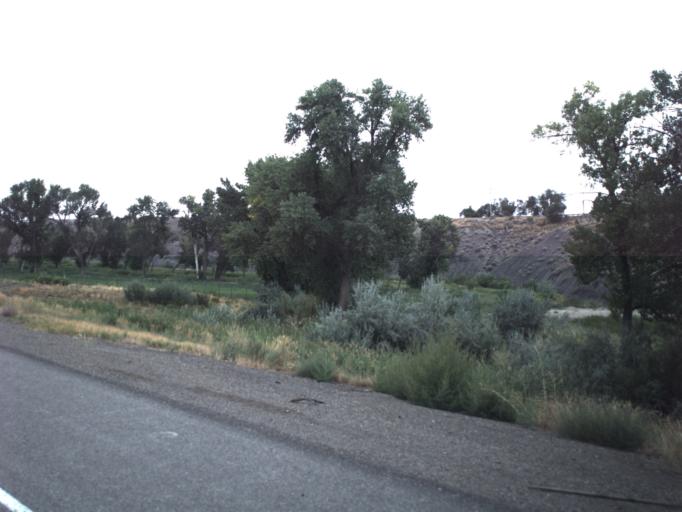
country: US
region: Utah
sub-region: Carbon County
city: Price
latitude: 39.5918
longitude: -110.8201
